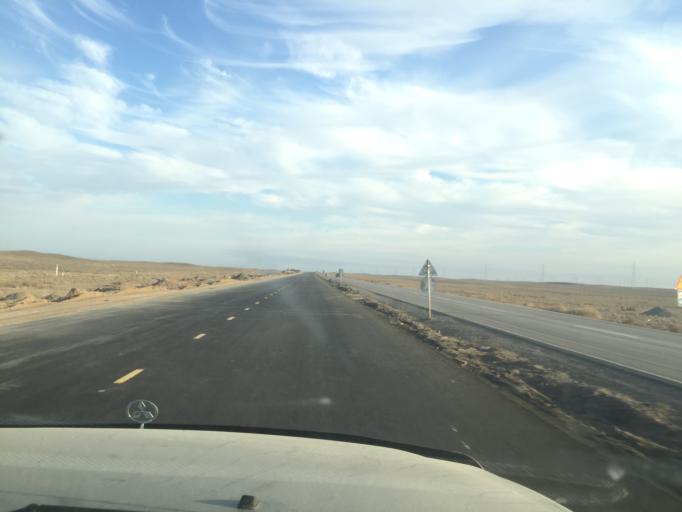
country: KZ
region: Almaty Oblysy
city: Ulken
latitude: 45.2310
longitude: 73.8428
